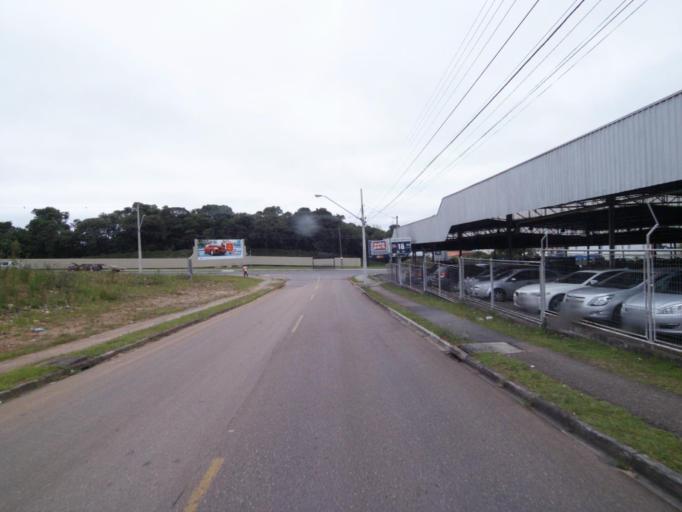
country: BR
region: Parana
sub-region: Sao Jose Dos Pinhais
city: Sao Jose dos Pinhais
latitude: -25.5364
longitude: -49.1859
